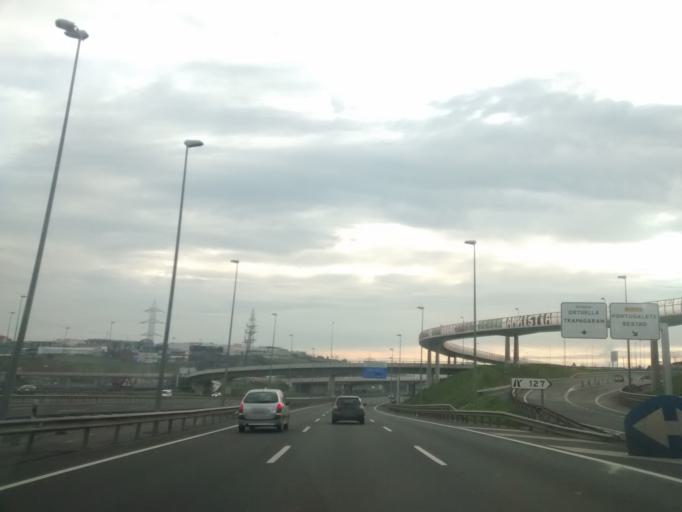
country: ES
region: Basque Country
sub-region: Bizkaia
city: Santurtzi
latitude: 43.3120
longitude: -3.0360
